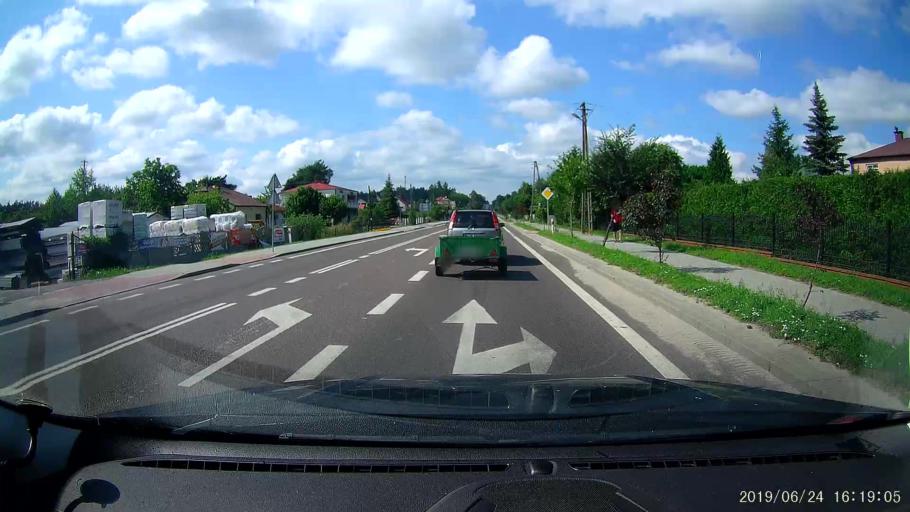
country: PL
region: Lublin Voivodeship
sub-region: Powiat tomaszowski
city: Belzec
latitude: 50.3854
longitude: 23.4380
